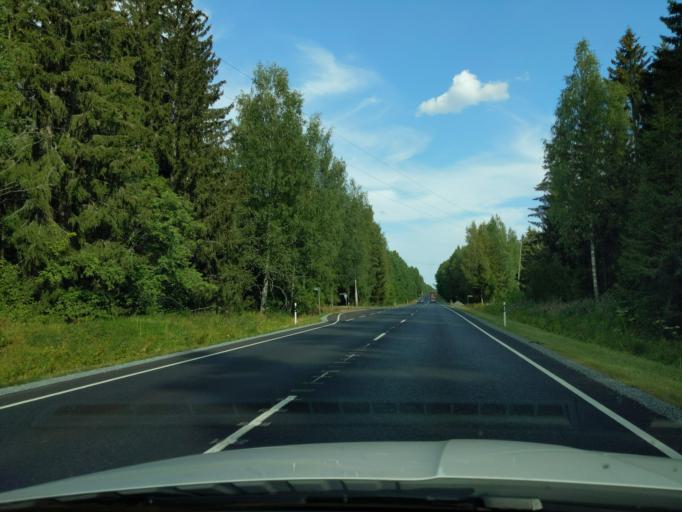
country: FI
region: Haeme
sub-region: Haemeenlinna
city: Hauho
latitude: 61.1607
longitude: 24.6762
